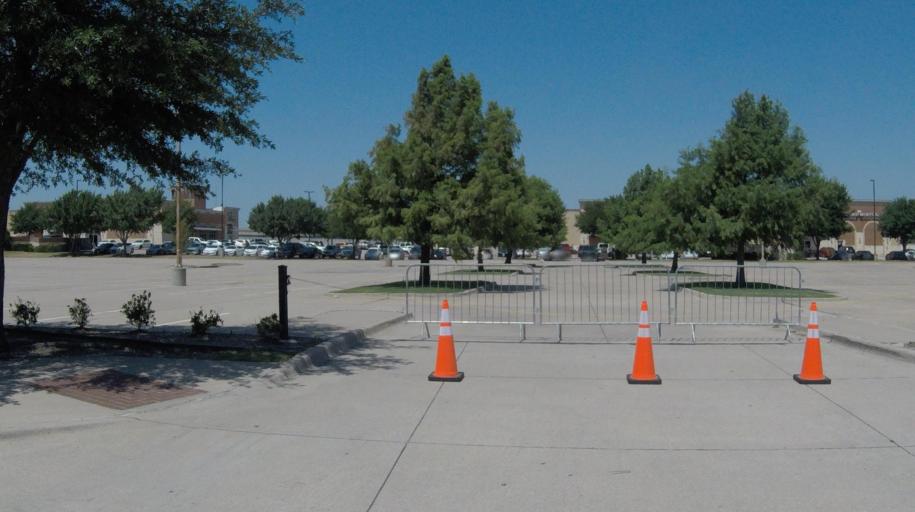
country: US
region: Texas
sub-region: Collin County
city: Frisco
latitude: 33.1554
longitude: -96.8380
